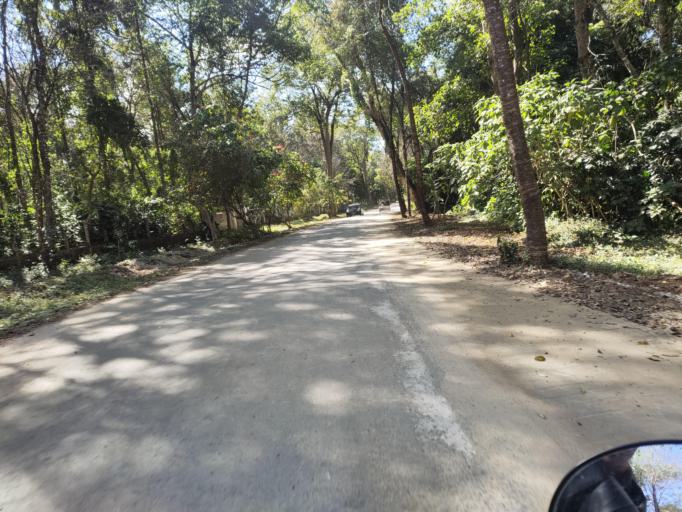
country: MM
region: Mandalay
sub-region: Pyin Oo Lwin District
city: Pyin Oo Lwin
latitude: 21.9877
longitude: 96.4692
